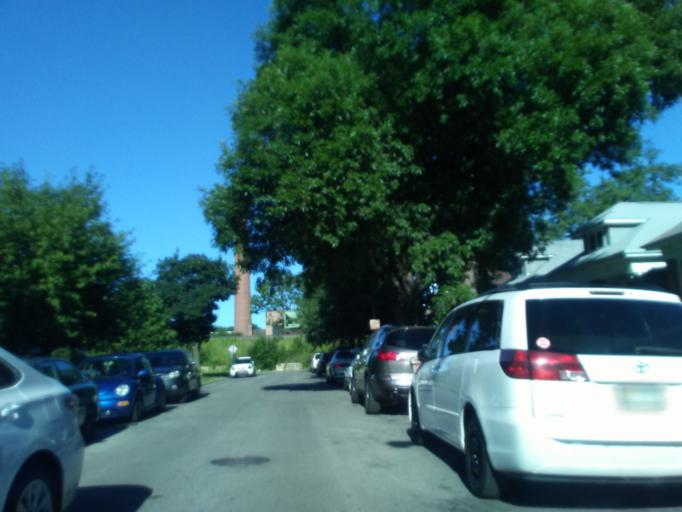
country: US
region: Illinois
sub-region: Cook County
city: Oak Park
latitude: 41.9197
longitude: -87.7426
